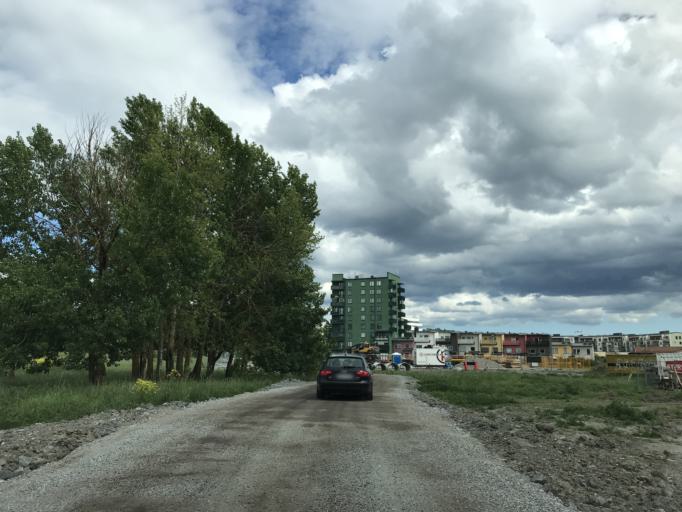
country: SE
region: Stockholm
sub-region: Solna Kommun
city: Rasunda
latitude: 59.3833
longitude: 17.9990
